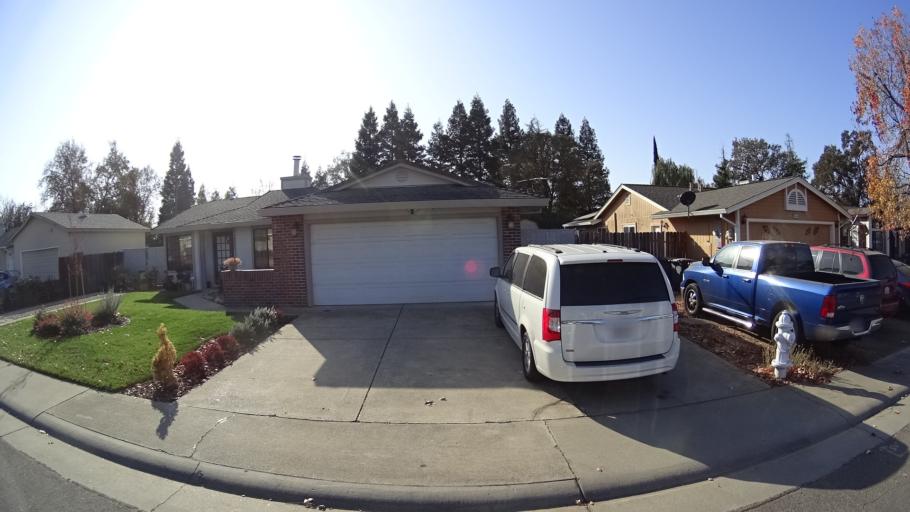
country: US
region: California
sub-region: Sacramento County
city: Citrus Heights
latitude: 38.6970
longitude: -121.2560
